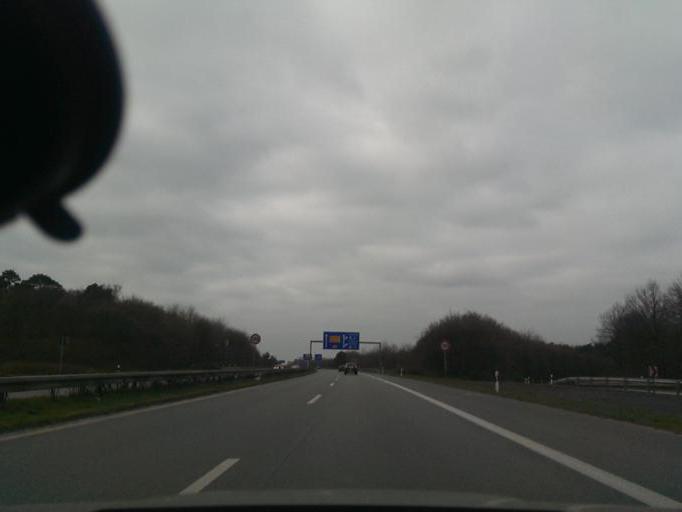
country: DE
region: North Rhine-Westphalia
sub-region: Regierungsbezirk Detmold
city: Rheda-Wiedenbruck
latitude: 51.8494
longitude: 8.3300
